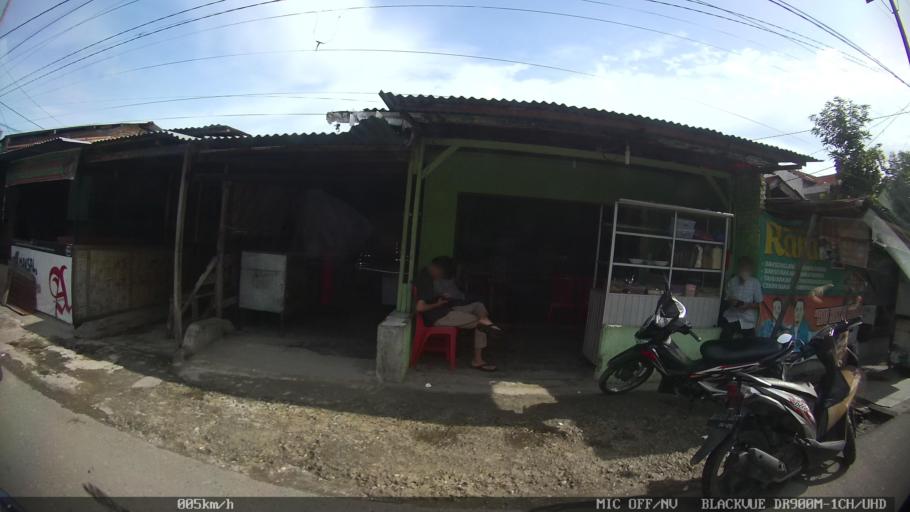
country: ID
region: North Sumatra
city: Medan
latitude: 3.6118
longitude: 98.6509
